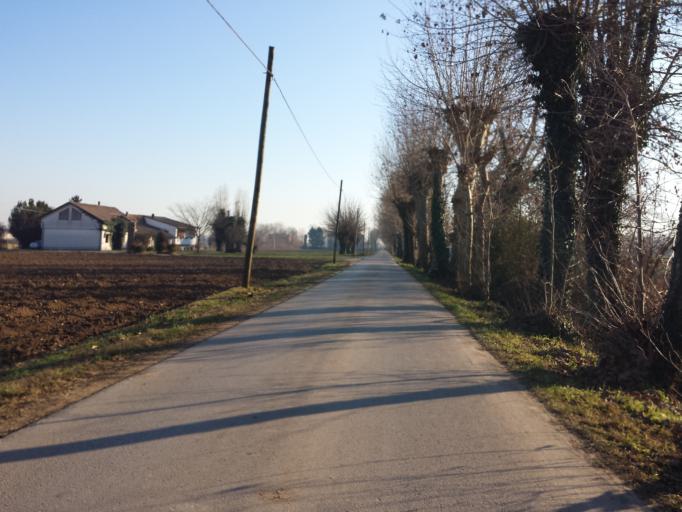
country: IT
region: Veneto
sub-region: Provincia di Vicenza
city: Sandrigo
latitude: 45.6425
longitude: 11.6018
